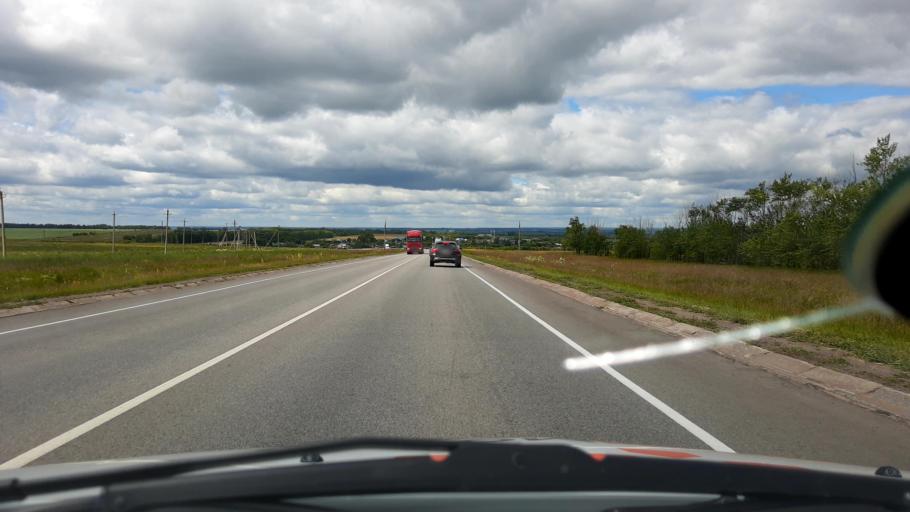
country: RU
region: Bashkortostan
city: Buzdyak
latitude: 54.6714
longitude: 54.7531
